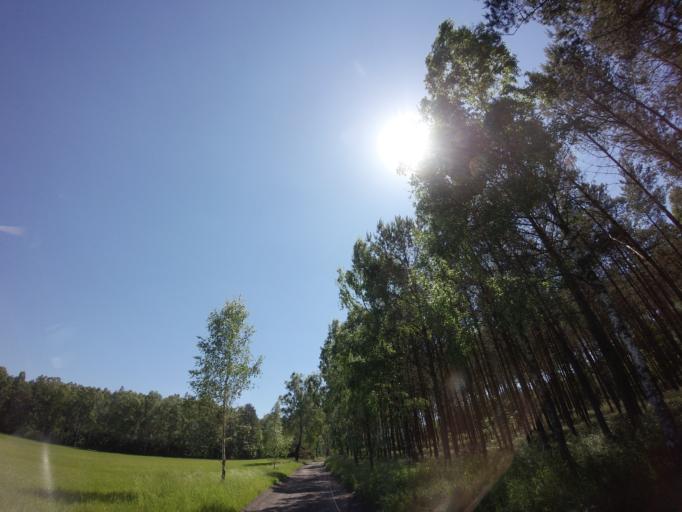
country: PL
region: West Pomeranian Voivodeship
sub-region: Powiat walecki
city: Miroslawiec
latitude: 53.2462
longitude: 16.0279
